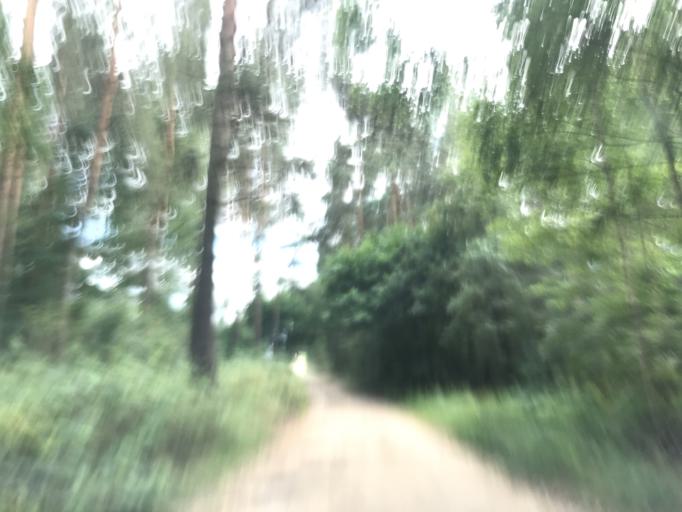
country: PL
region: Kujawsko-Pomorskie
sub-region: Powiat brodnicki
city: Brzozie
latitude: 53.3240
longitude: 19.6883
